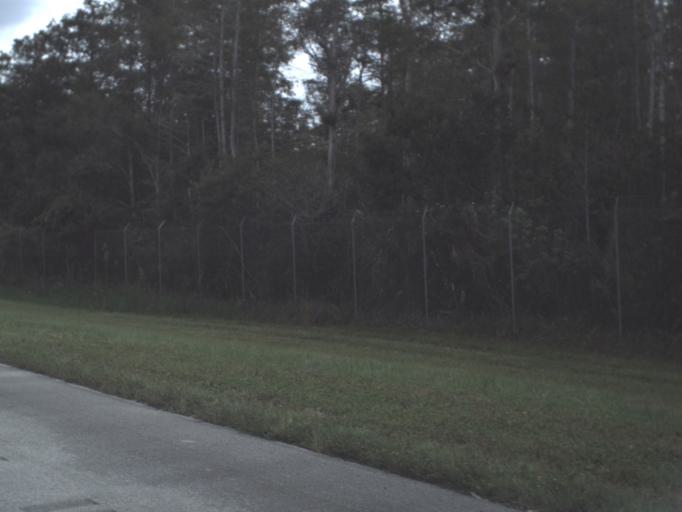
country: US
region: Florida
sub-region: Collier County
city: Immokalee
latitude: 26.1672
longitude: -81.1698
